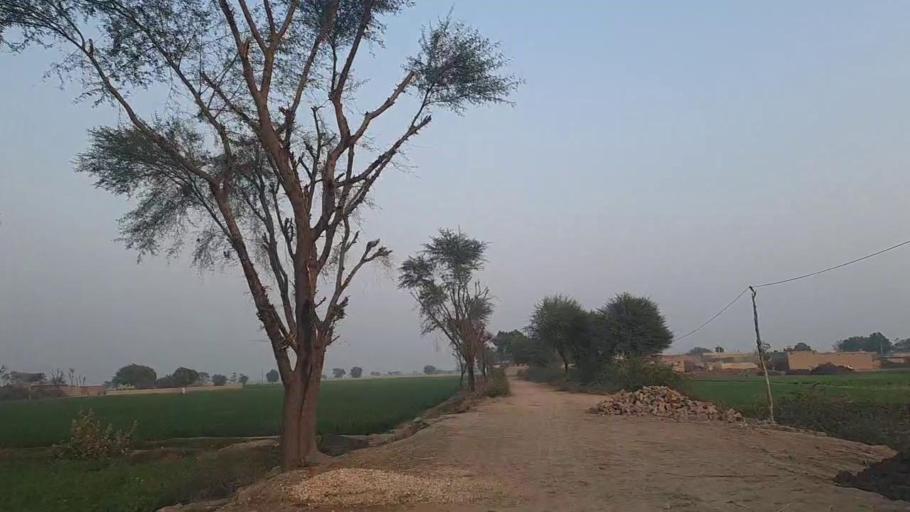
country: PK
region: Sindh
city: Nawabshah
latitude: 26.2577
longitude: 68.4590
